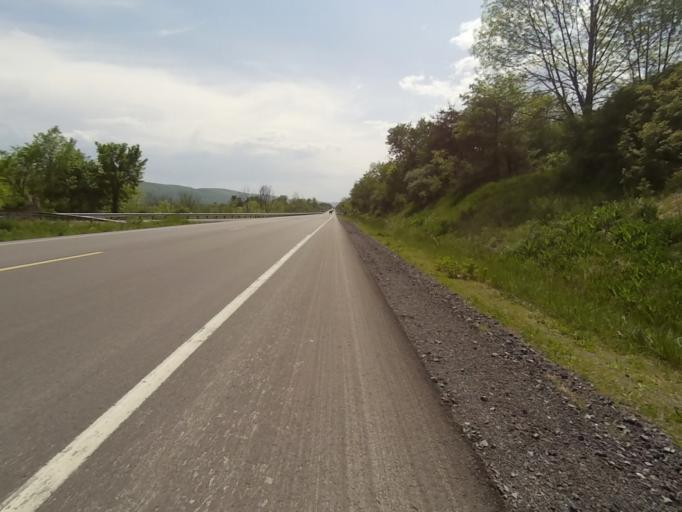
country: US
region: Pennsylvania
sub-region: Centre County
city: Zion
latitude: 41.0251
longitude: -77.6665
